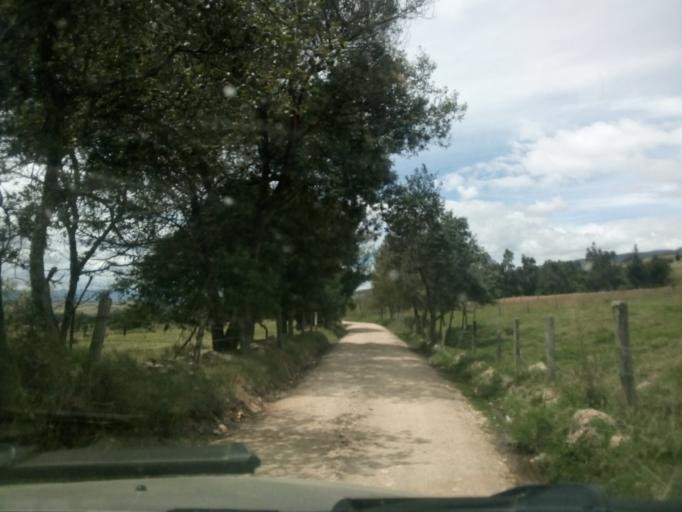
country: CO
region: Boyaca
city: Toca
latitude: 5.6039
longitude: -73.1525
